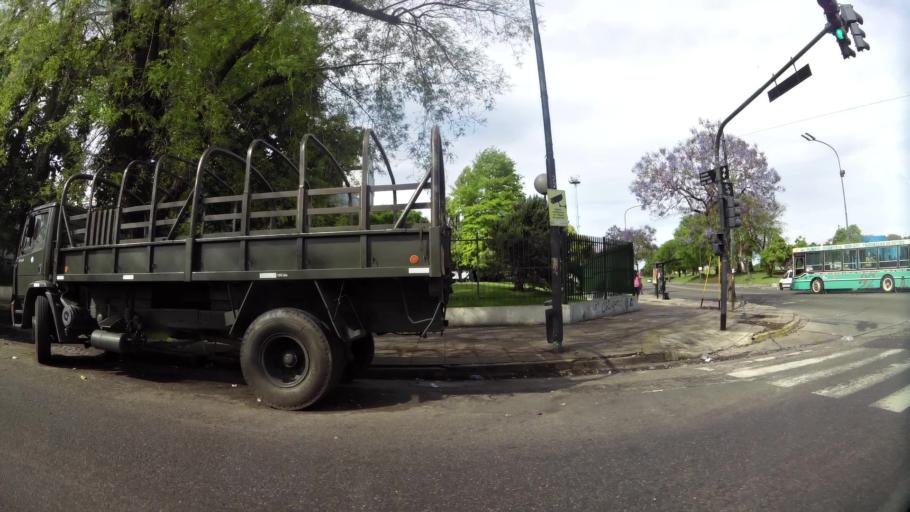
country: AR
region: Buenos Aires F.D.
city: Villa Lugano
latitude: -34.6601
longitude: -58.5033
